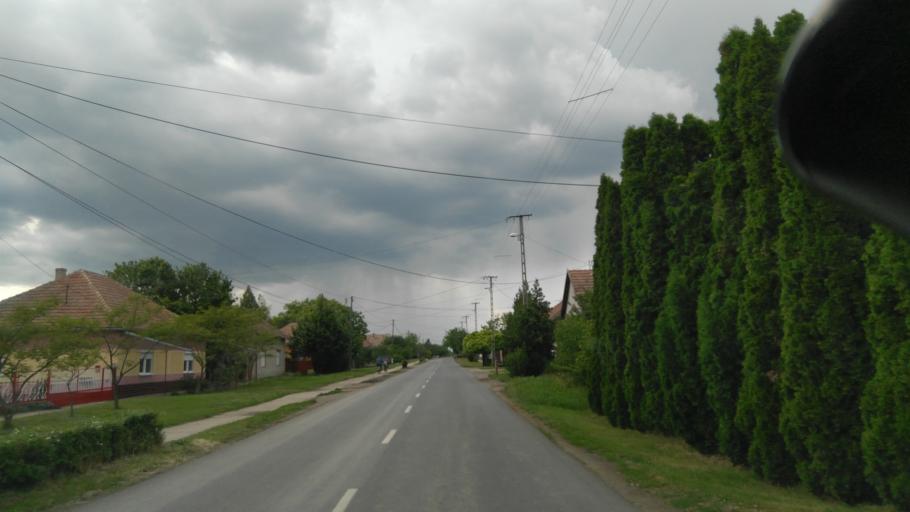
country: HU
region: Bekes
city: Dombegyhaz
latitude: 46.3441
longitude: 21.1264
